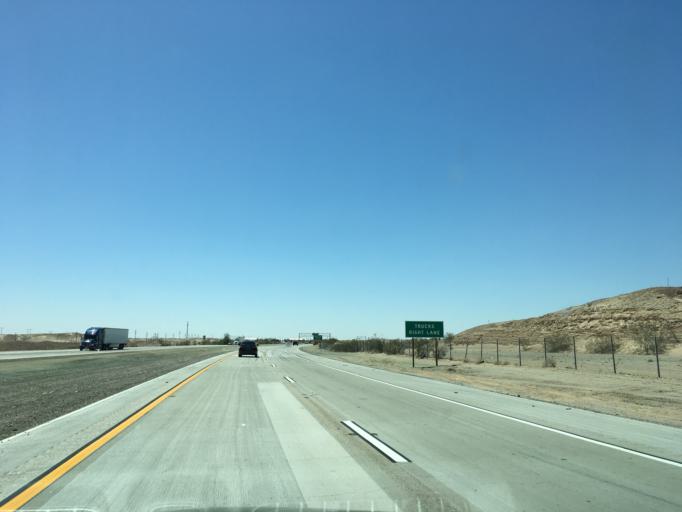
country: MX
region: Baja California
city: Los Algodones
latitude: 32.7448
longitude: -114.7301
